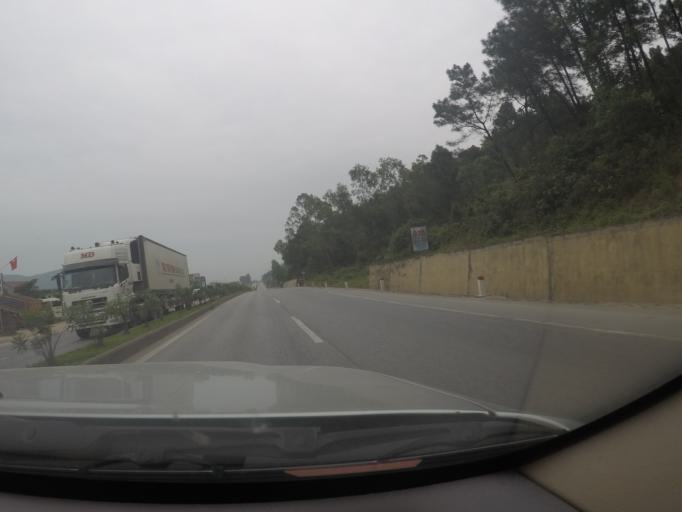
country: VN
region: Nghe An
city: Quan Hanh
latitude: 18.8647
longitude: 105.6335
